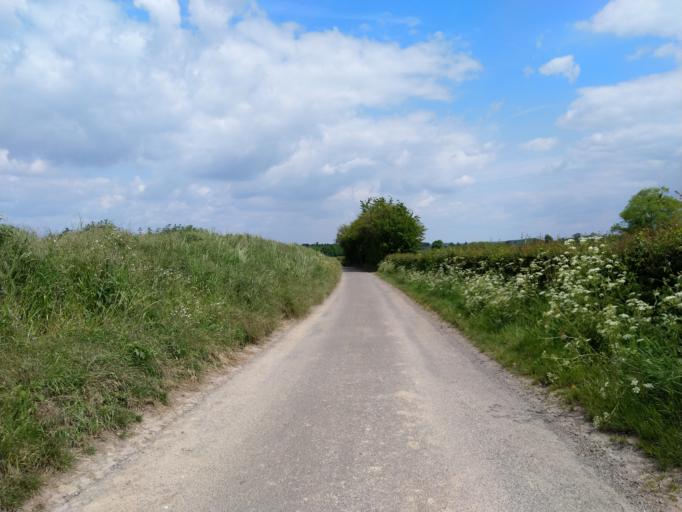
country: FR
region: Nord-Pas-de-Calais
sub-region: Departement du Nord
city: Le Quesnoy
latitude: 50.2476
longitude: 3.6569
